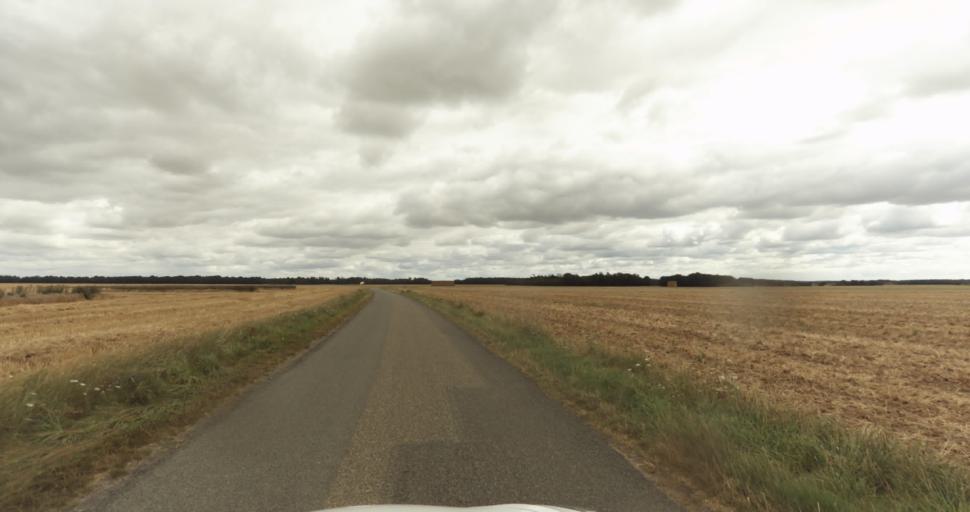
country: FR
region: Haute-Normandie
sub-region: Departement de l'Eure
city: Nonancourt
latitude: 48.8131
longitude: 1.1499
